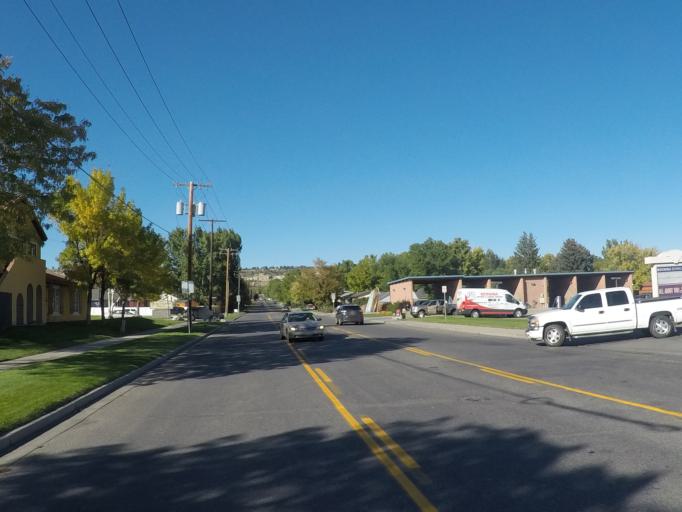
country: US
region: Montana
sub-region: Yellowstone County
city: Billings
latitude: 45.7846
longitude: -108.5903
